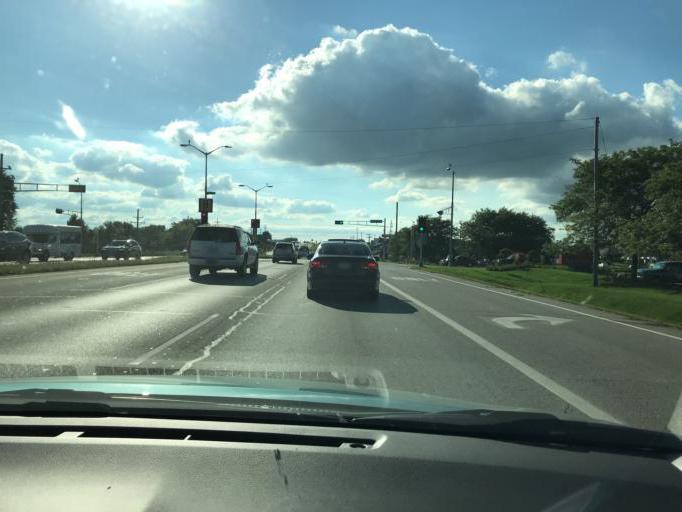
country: US
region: Wisconsin
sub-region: Kenosha County
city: Pleasant Prairie
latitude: 42.5670
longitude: -87.8909
